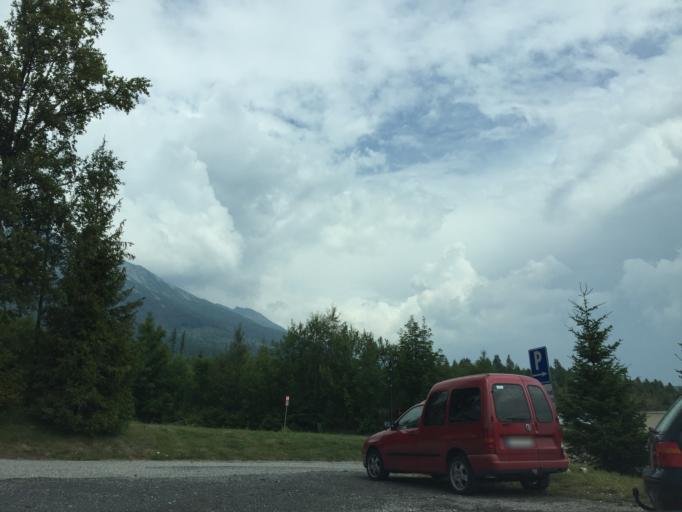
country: SK
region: Presovsky
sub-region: Okres Poprad
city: Vysoke Tatry
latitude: 49.1292
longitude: 20.2007
